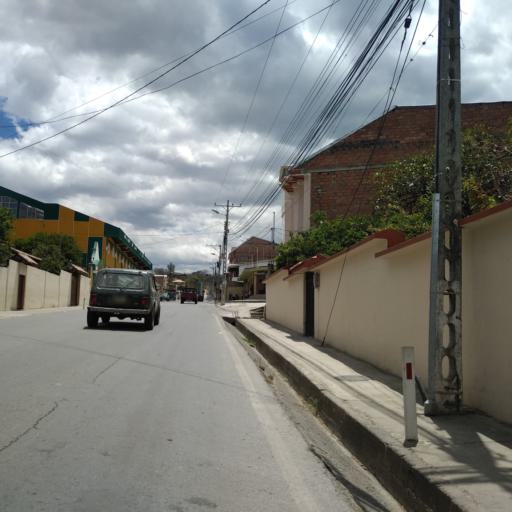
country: EC
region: Loja
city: Loja
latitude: -4.2191
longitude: -79.2574
